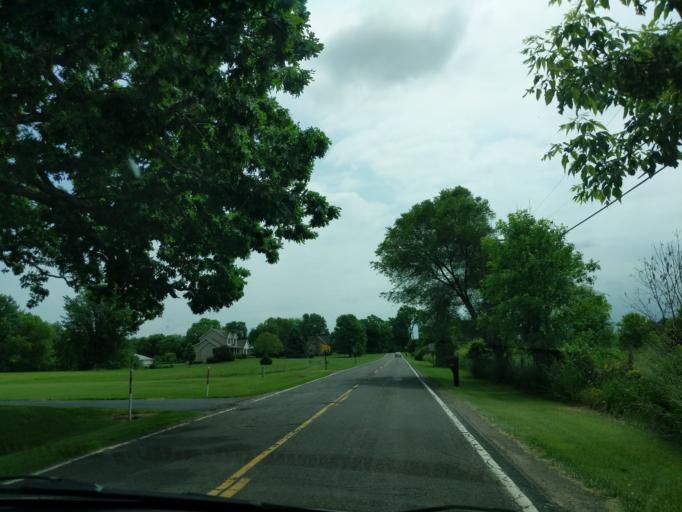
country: US
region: Michigan
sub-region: Ingham County
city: Williamston
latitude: 42.6938
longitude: -84.2622
